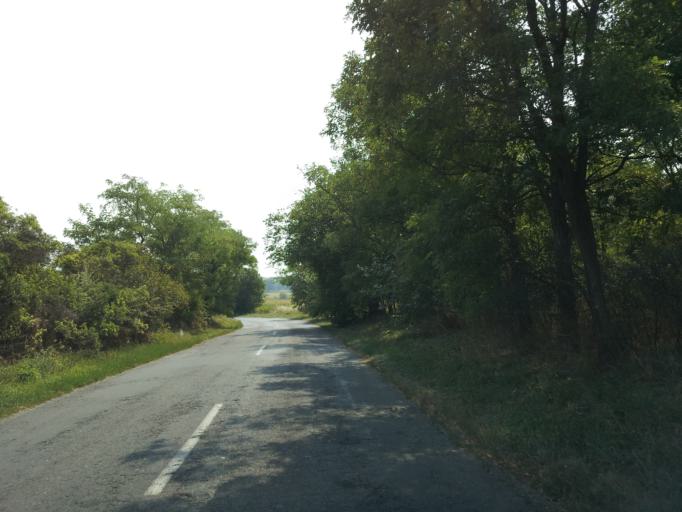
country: HU
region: Gyor-Moson-Sopron
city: Pannonhalma
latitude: 47.5115
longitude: 17.7693
